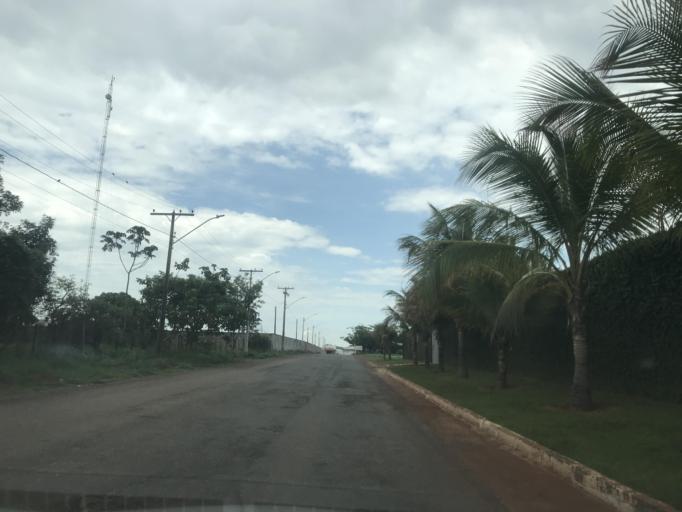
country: BR
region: Goias
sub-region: Luziania
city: Luziania
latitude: -16.2572
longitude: -47.9733
